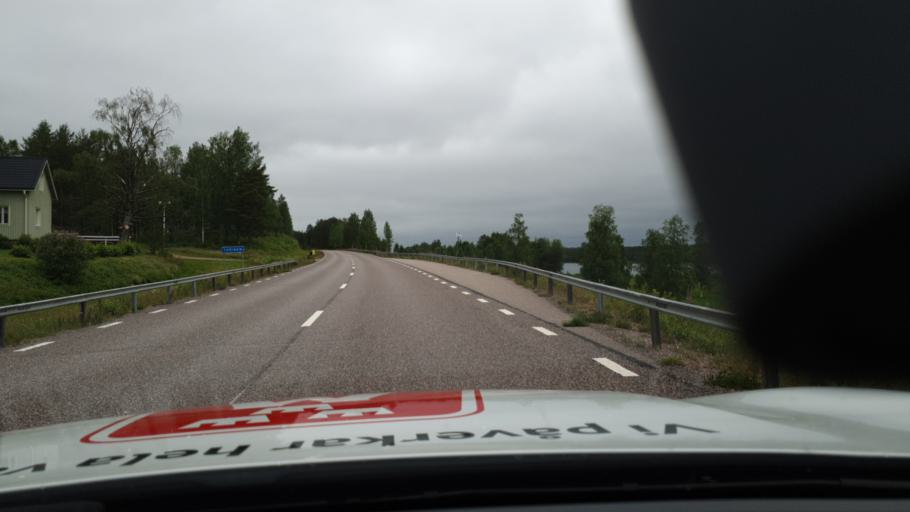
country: FI
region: Lapland
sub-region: Tunturi-Lappi
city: Kolari
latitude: 67.0305
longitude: 23.7162
